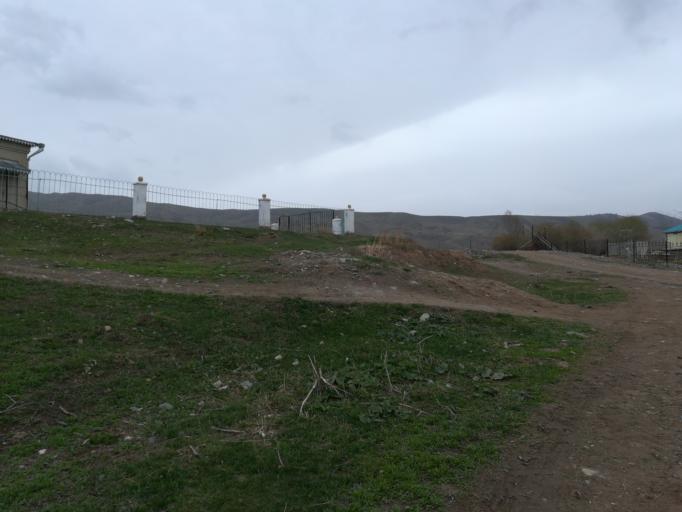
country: KG
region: Naryn
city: Naryn
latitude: 41.5165
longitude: 76.4383
